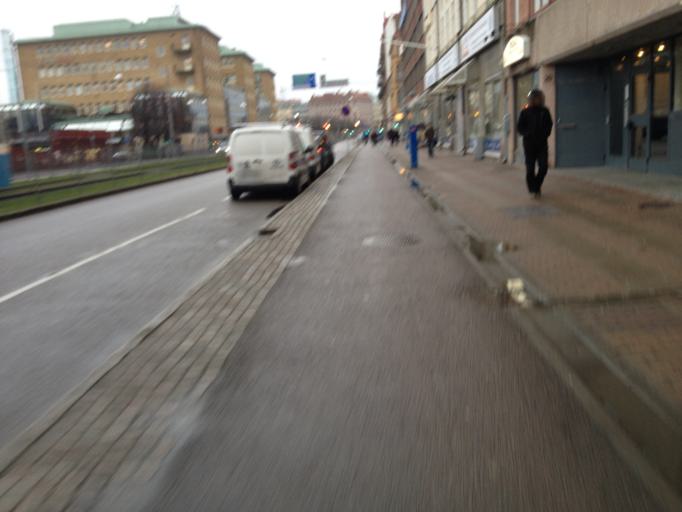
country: SE
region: Vaestra Goetaland
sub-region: Goteborg
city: Goeteborg
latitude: 57.6997
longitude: 11.9475
